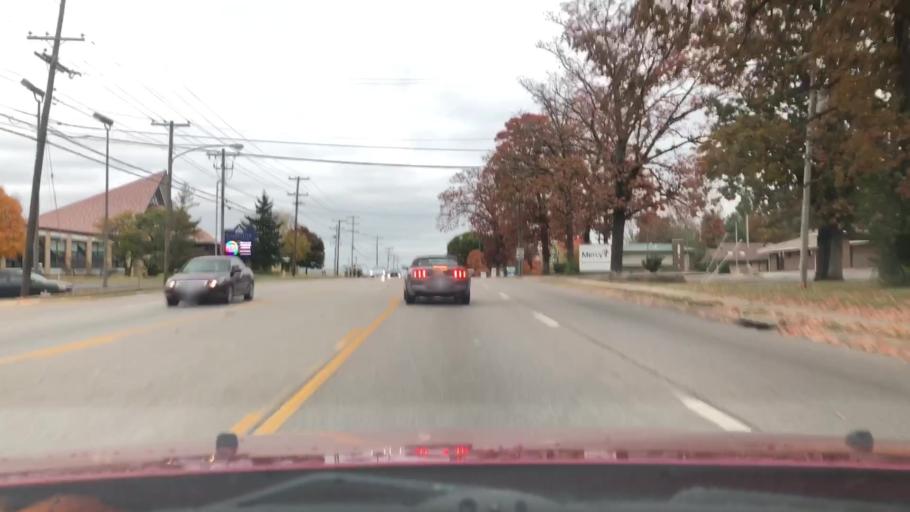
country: US
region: Missouri
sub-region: Greene County
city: Springfield
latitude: 37.1808
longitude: -93.2419
